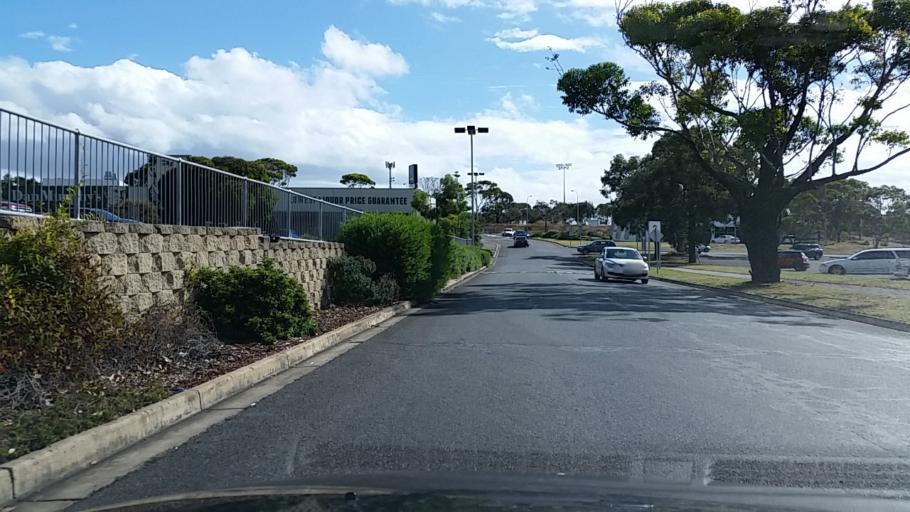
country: AU
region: South Australia
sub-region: Onkaparinga
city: Noarlunga Downs
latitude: -35.1430
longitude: 138.4960
